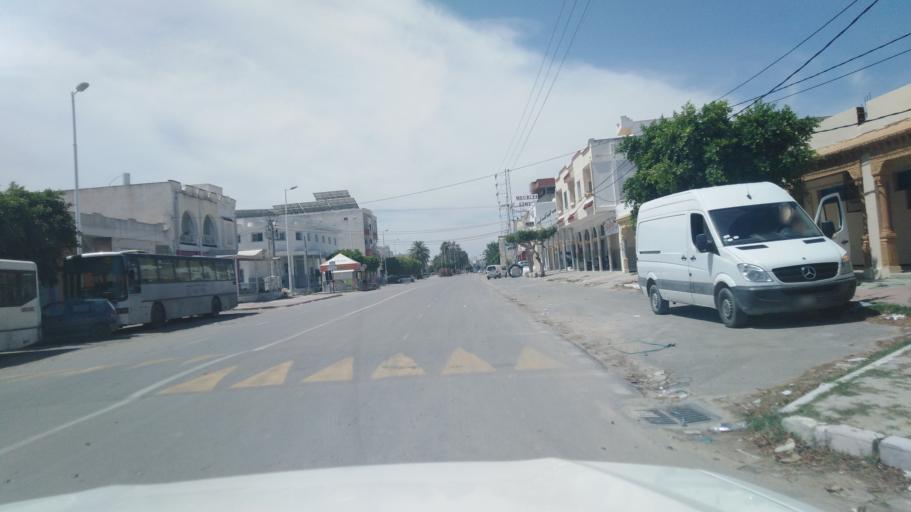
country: TN
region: Al Mahdiyah
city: Ksour Essaf
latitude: 35.4279
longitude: 11.0009
